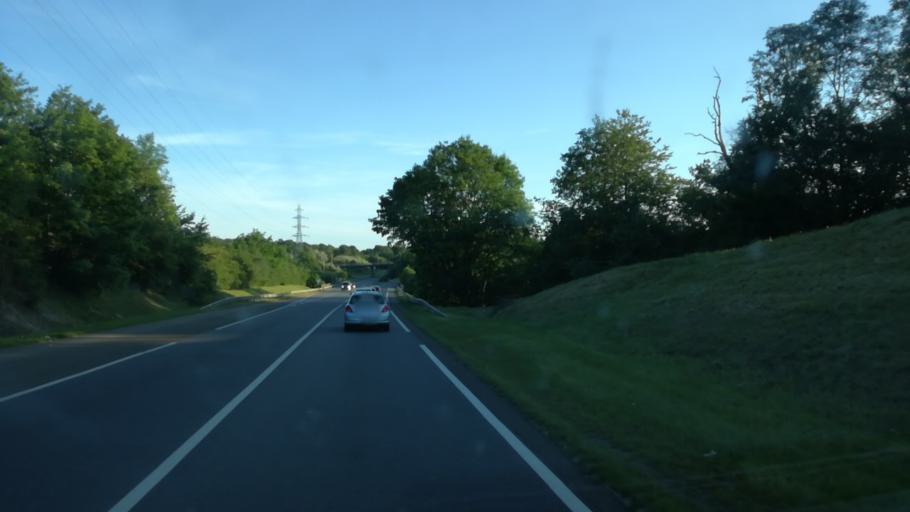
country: FR
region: Ile-de-France
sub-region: Departement des Yvelines
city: Elancourt
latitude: 48.7801
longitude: 1.9720
